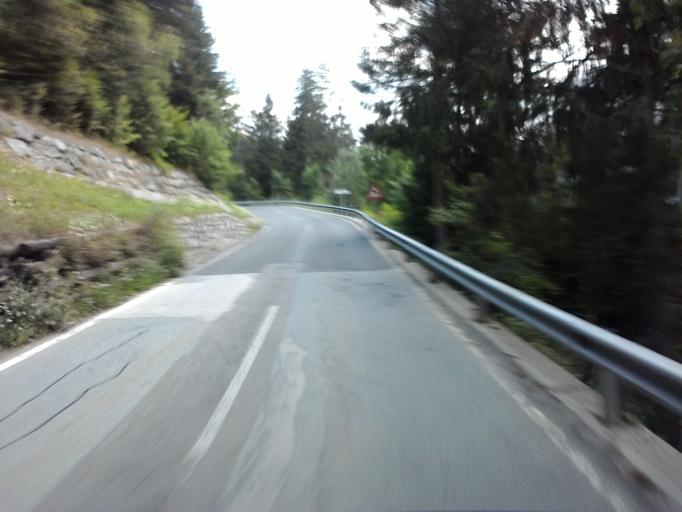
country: AT
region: Carinthia
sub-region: Politischer Bezirk Spittal an der Drau
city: Oberdrauburg
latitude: 46.6814
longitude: 12.9549
